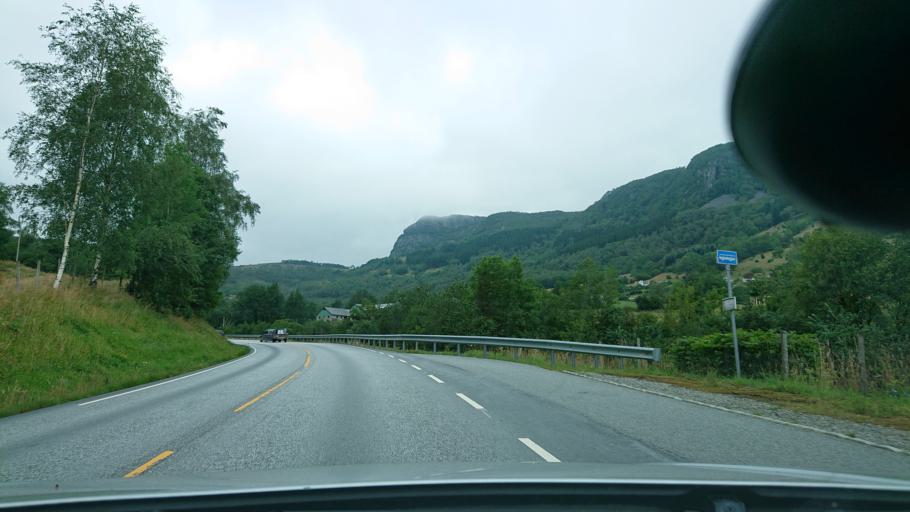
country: NO
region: Rogaland
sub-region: Hjelmeland
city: Hjelmelandsvagen
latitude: 59.1648
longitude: 6.1705
